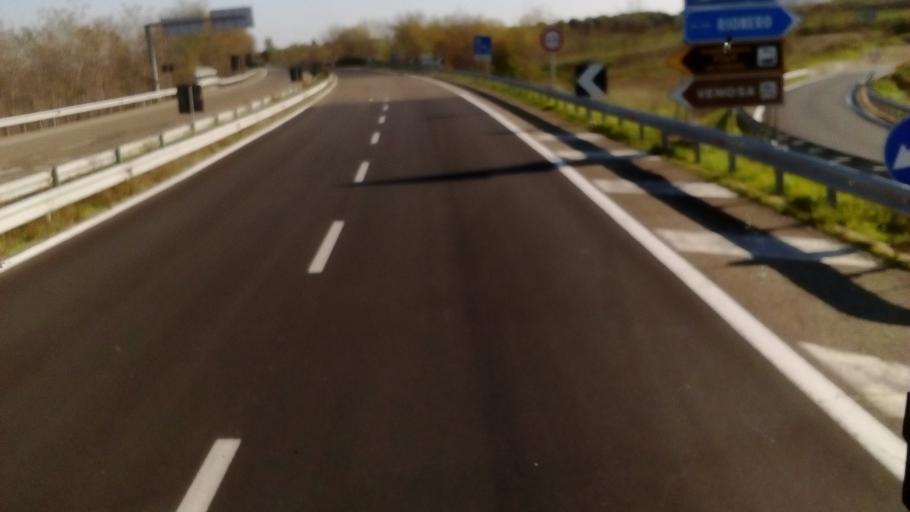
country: IT
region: Basilicate
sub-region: Provincia di Potenza
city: Zona 179
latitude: 41.0835
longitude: 15.6067
